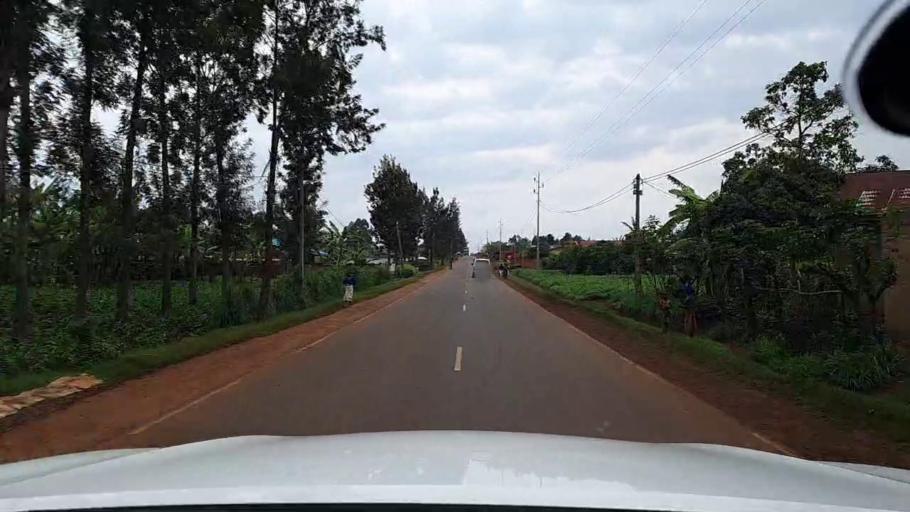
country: RW
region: Western Province
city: Cyangugu
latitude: -2.6330
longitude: 28.9519
